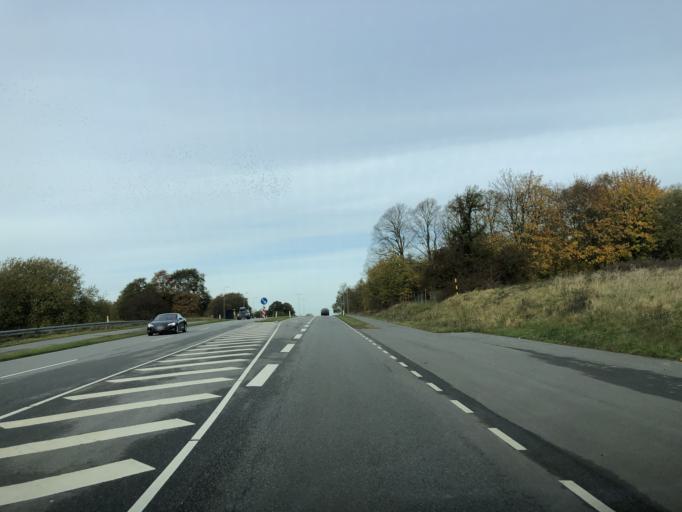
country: DK
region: Capital Region
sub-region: Rudersdal Kommune
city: Birkerod
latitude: 55.8566
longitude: 12.4068
